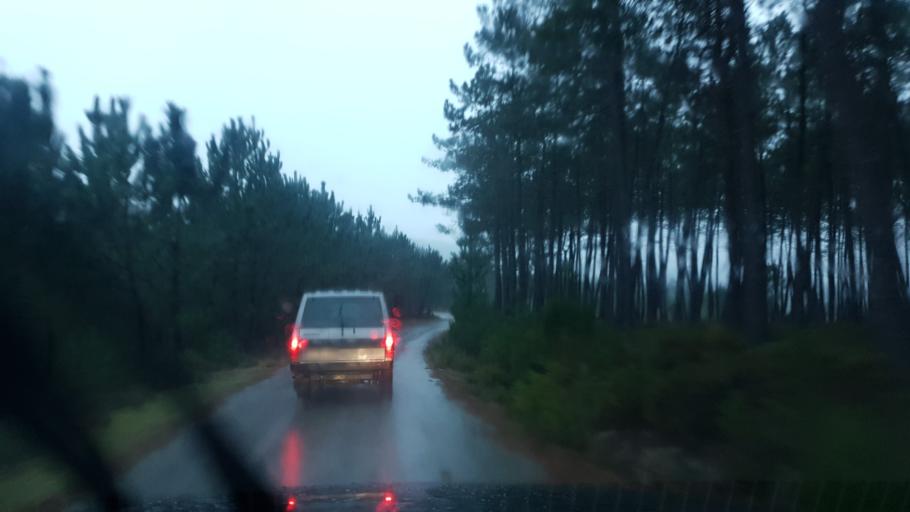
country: PT
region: Viseu
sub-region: Sao Pedro do Sul
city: Sao Pedro do Sul
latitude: 40.8274
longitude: -8.1364
